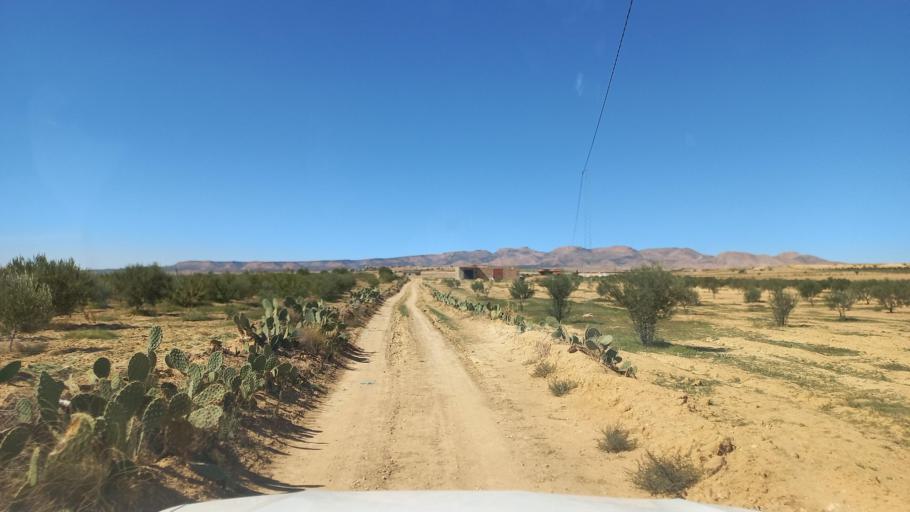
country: TN
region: Al Qasrayn
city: Sbiba
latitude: 35.3659
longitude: 9.0888
